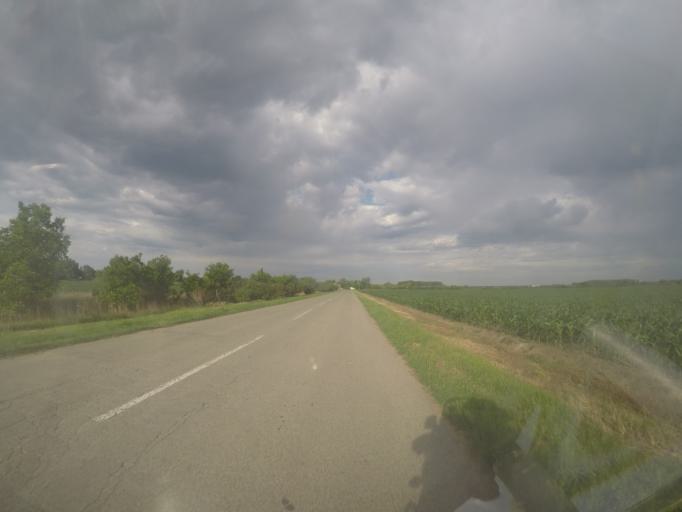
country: RS
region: Central Serbia
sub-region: Belgrade
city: Zemun
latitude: 44.9127
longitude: 20.4322
